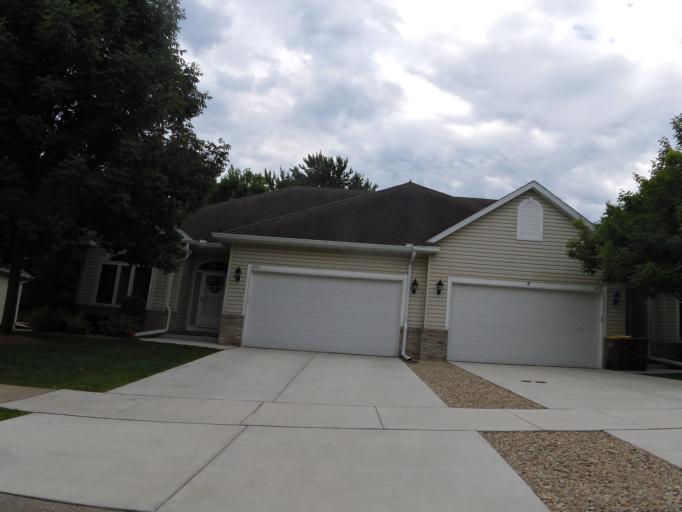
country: US
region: Minnesota
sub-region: Scott County
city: Prior Lake
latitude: 44.7099
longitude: -93.4337
